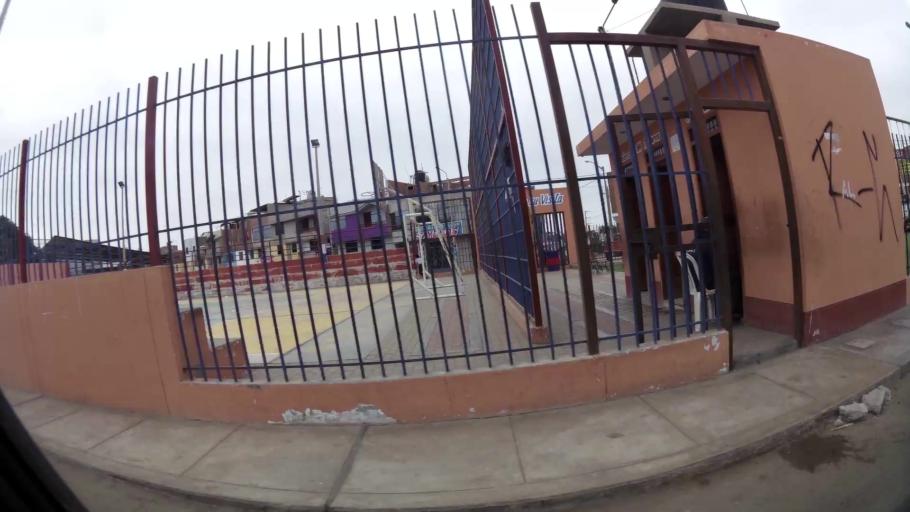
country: PE
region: La Libertad
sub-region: Provincia de Trujillo
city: La Esperanza
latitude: -8.0813
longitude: -79.0518
